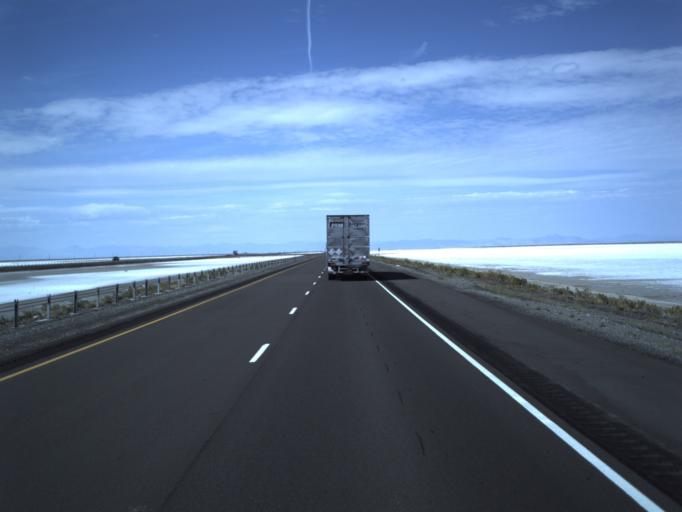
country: US
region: Utah
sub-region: Tooele County
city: Wendover
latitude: 40.7293
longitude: -113.3948
